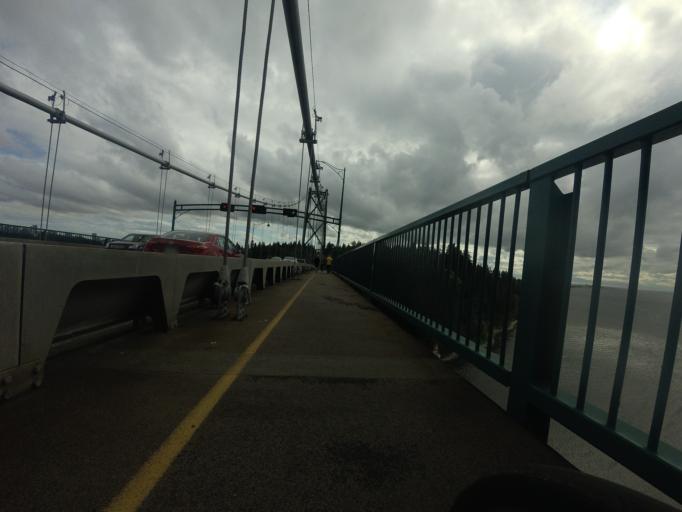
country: CA
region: British Columbia
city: West End
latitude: 49.3163
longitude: -123.1380
